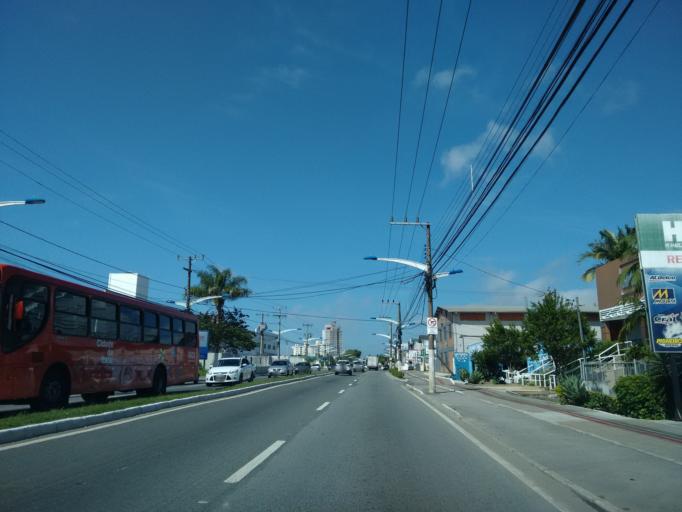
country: BR
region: Santa Catarina
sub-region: Itajai
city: Itajai
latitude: -26.9319
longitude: -48.6883
